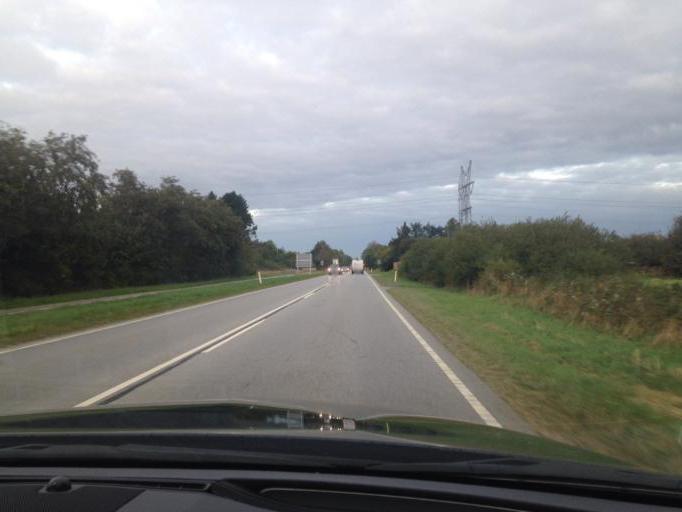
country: DK
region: South Denmark
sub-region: Haderslev Kommune
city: Vojens
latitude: 55.2528
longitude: 9.3535
